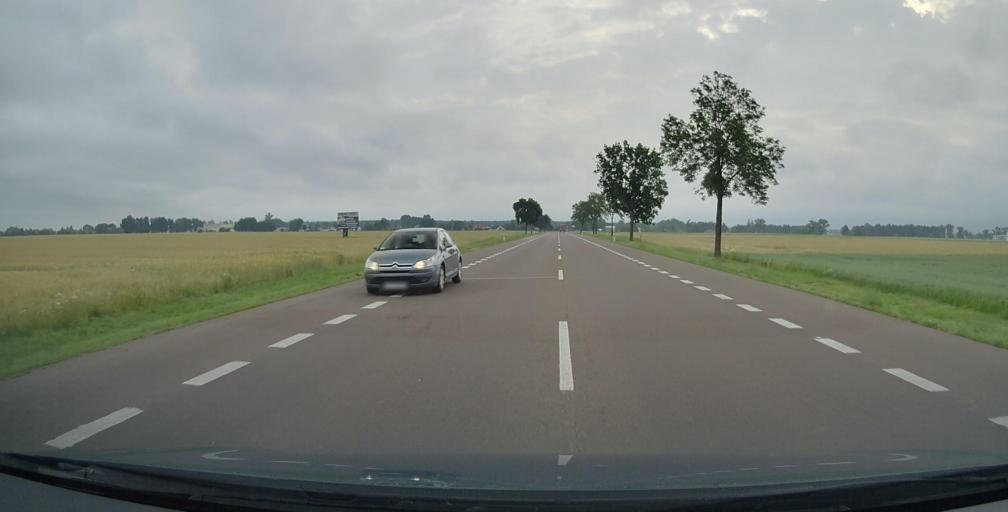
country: PL
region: Lublin Voivodeship
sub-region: Powiat bialski
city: Miedzyrzec Podlaski
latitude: 52.0233
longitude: 22.8584
